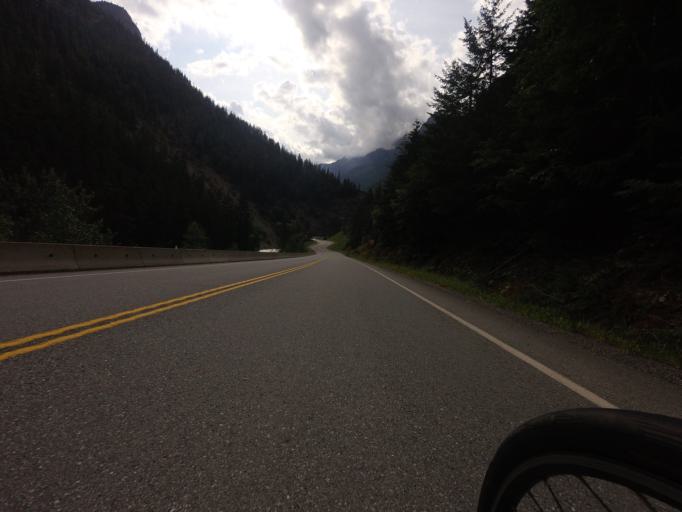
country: CA
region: British Columbia
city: Lillooet
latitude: 50.6442
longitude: -122.0579
